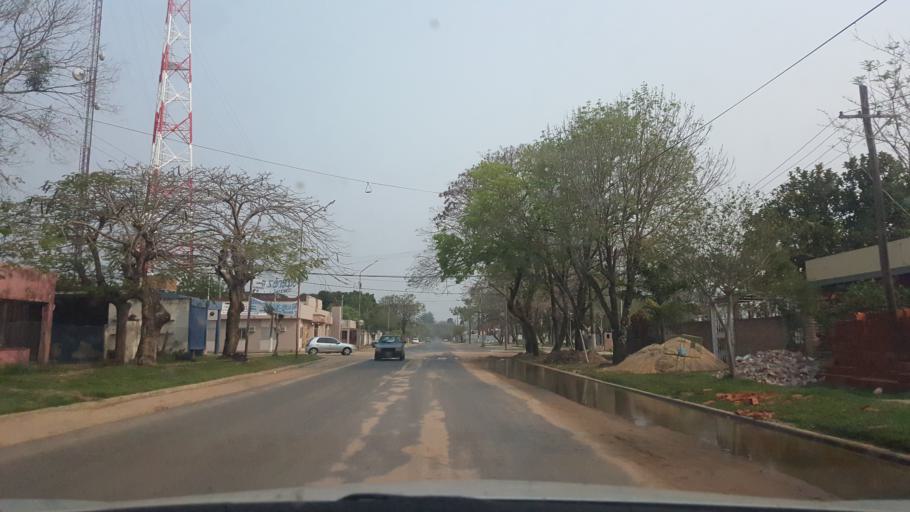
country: AR
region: Corrientes
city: Ita Ibate
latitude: -27.4250
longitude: -57.3375
